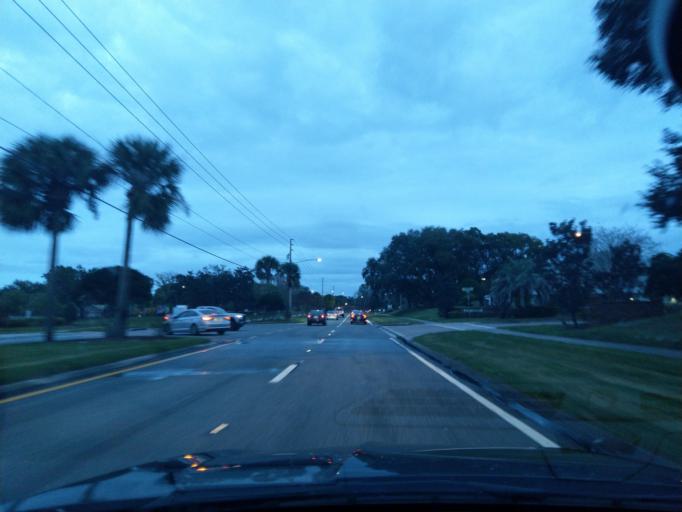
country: US
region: Florida
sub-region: Orange County
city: Williamsburg
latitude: 28.3969
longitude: -81.4234
